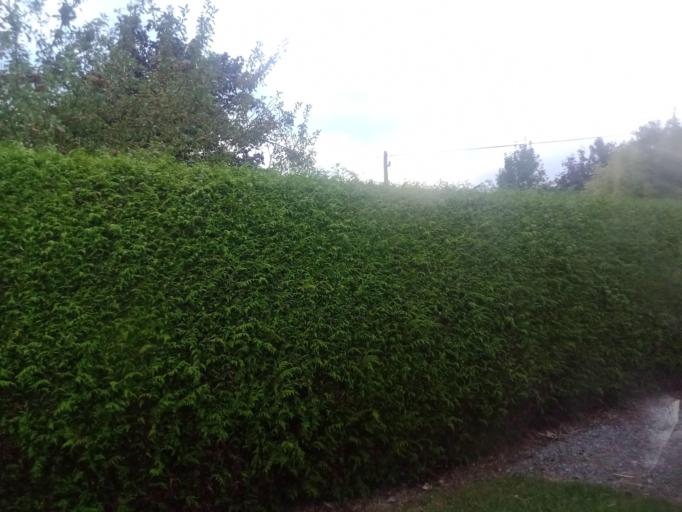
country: IE
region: Leinster
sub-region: Laois
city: Mountmellick
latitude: 53.1078
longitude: -7.3417
